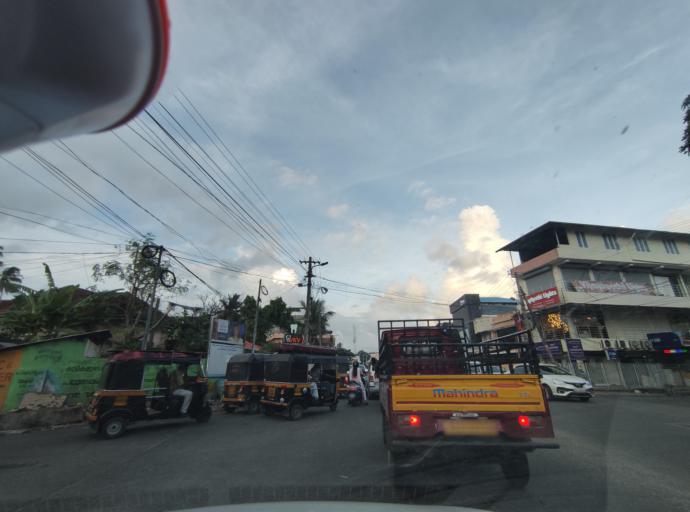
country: IN
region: Kerala
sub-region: Thiruvananthapuram
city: Thiruvananthapuram
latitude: 8.4865
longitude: 76.9444
